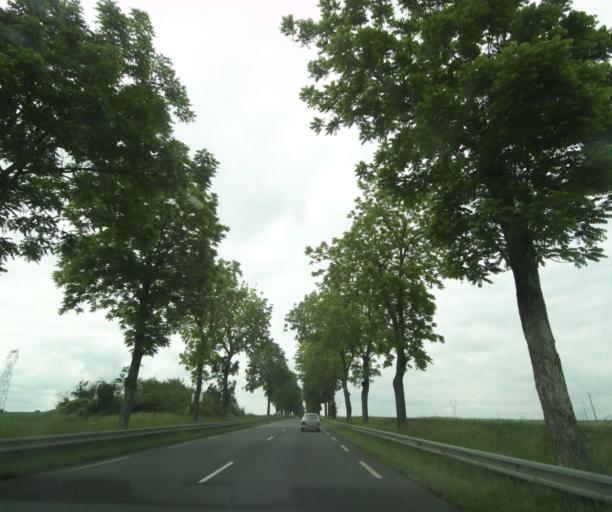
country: FR
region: Pays de la Loire
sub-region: Departement de Maine-et-Loire
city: Distre
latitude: 47.2083
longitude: -0.1189
